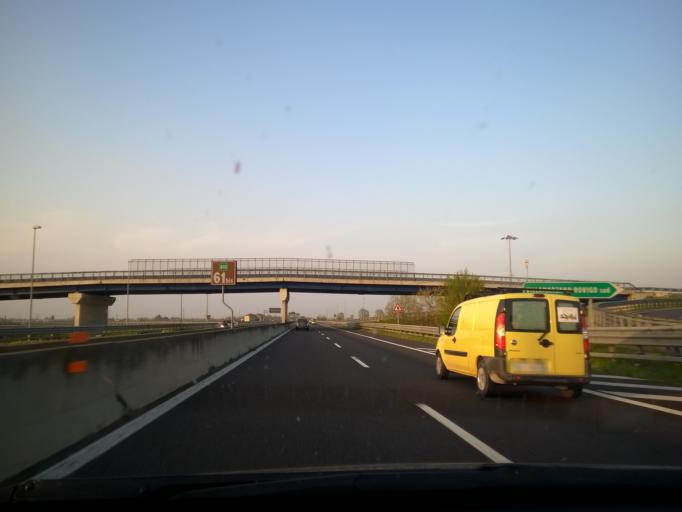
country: IT
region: Veneto
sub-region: Provincia di Rovigo
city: Villamarzana
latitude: 45.0238
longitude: 11.6953
